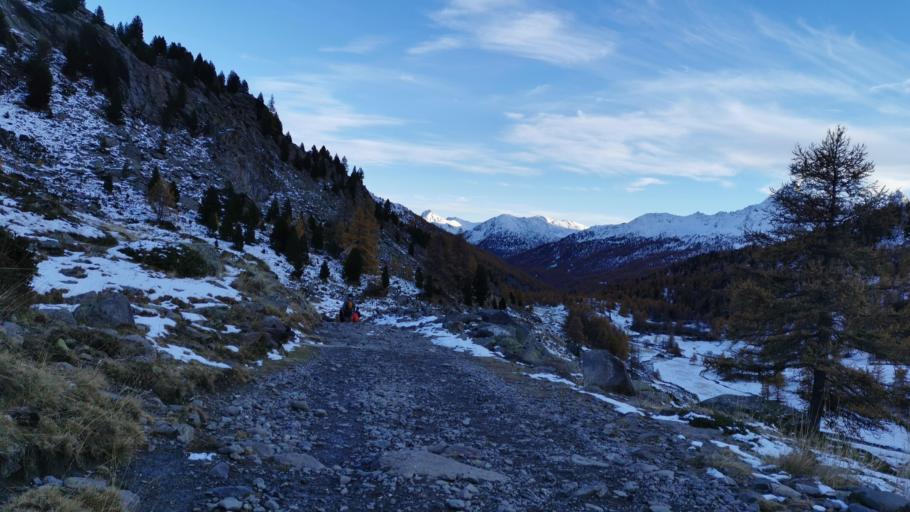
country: FR
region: Provence-Alpes-Cote d'Azur
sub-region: Departement des Hautes-Alpes
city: Le Monetier-les-Bains
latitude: 45.0658
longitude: 6.5201
